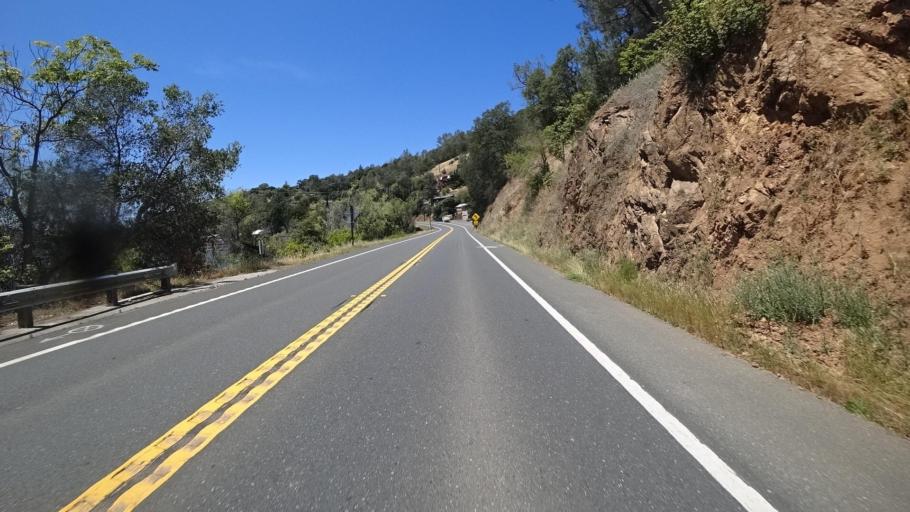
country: US
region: California
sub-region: Lake County
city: Clearlake Oaks
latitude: 39.0205
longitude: -122.6879
